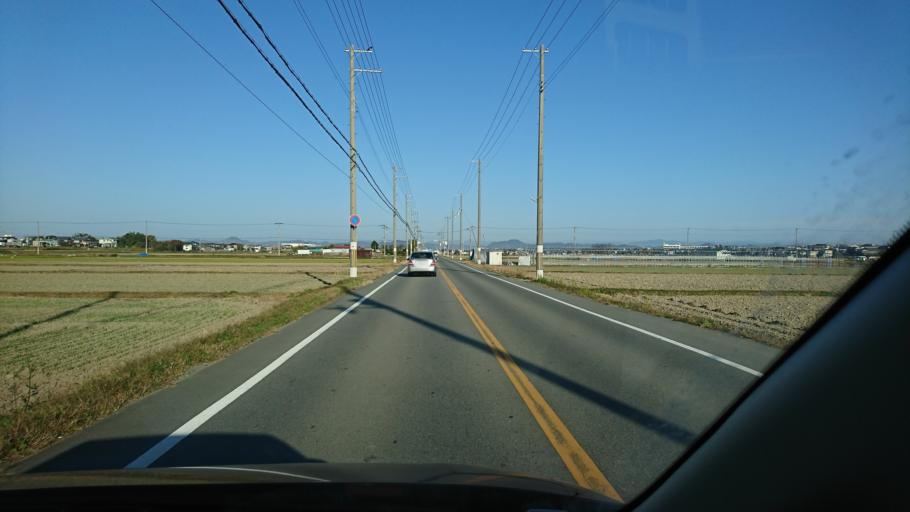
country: JP
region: Hyogo
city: Kakogawacho-honmachi
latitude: 34.7376
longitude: 134.9048
